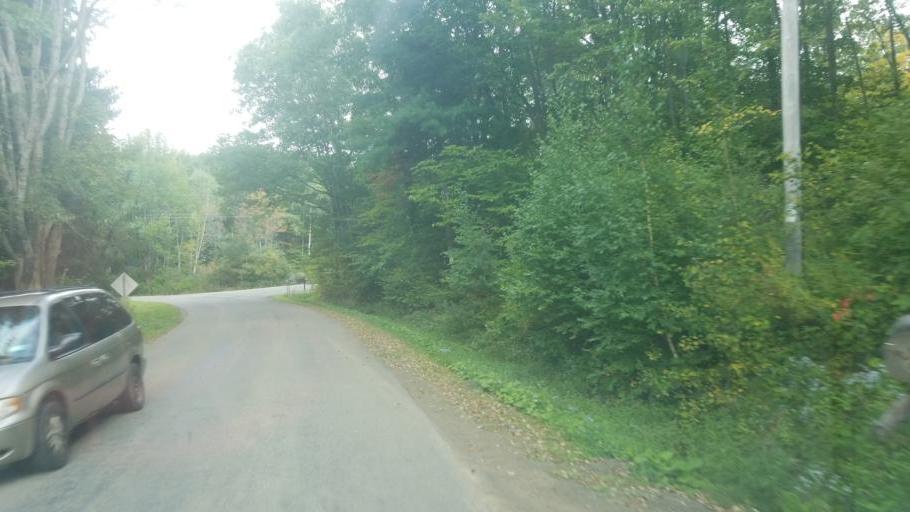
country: US
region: New York
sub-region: Cattaraugus County
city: Weston Mills
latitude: 42.1606
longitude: -78.3621
